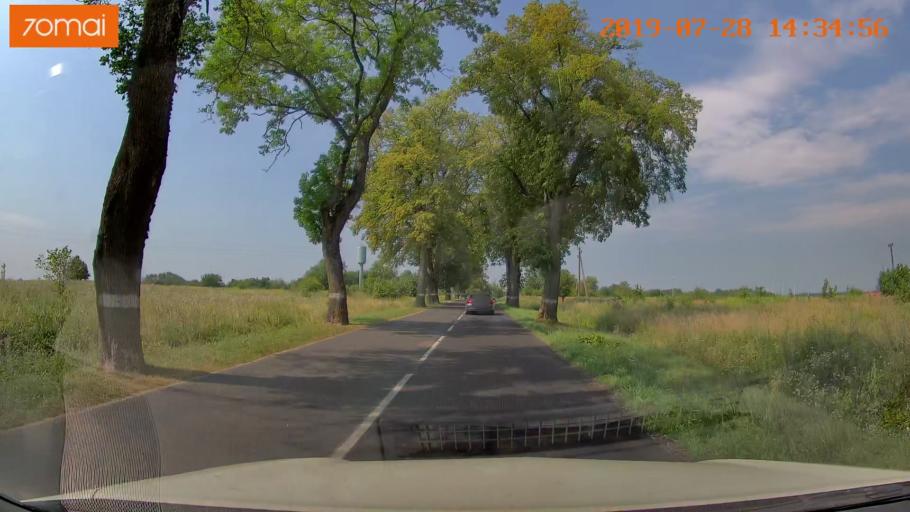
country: RU
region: Kaliningrad
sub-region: Gorod Kaliningrad
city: Yantarnyy
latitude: 54.8280
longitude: 20.0130
